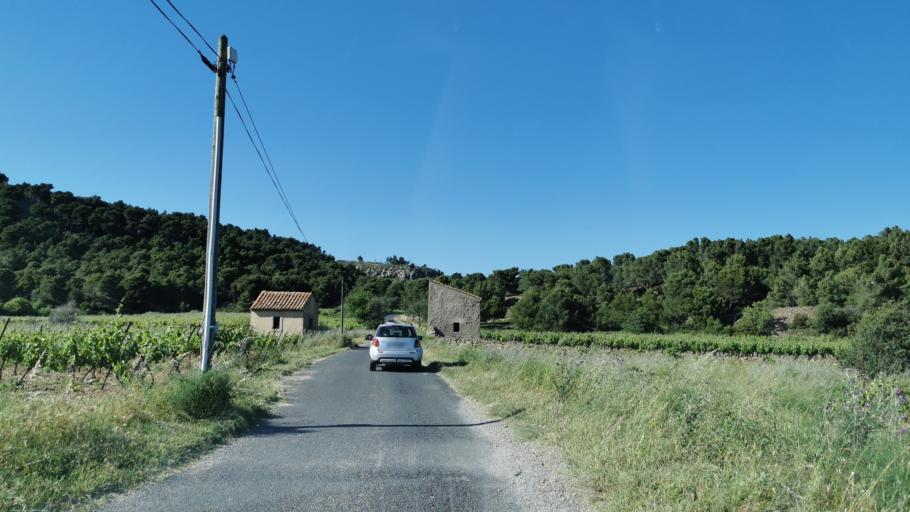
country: FR
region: Languedoc-Roussillon
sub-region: Departement de l'Aude
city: Gruissan
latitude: 43.1249
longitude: 3.0952
